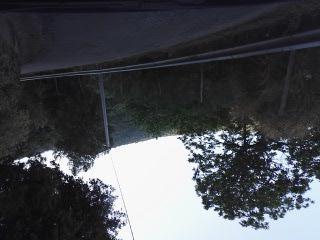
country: IT
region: Calabria
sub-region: Provincia di Vibo-Valentia
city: Nardodipace
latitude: 38.4387
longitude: 16.3391
